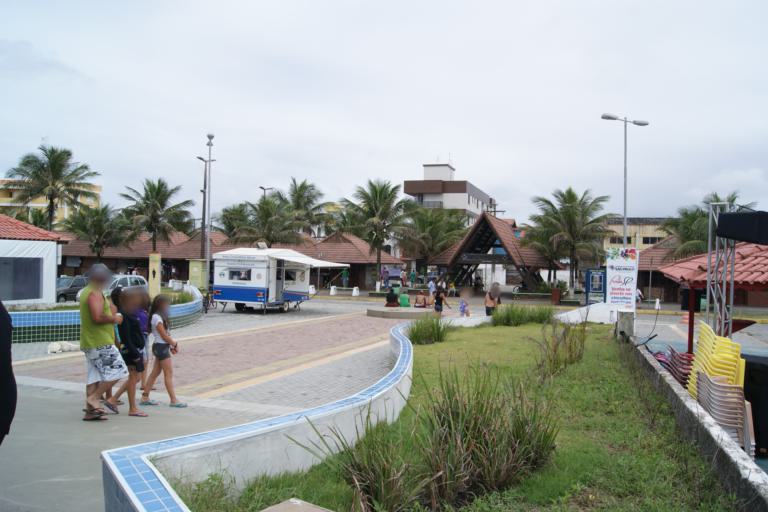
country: BR
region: Sao Paulo
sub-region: Mongagua
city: Mongagua
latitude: -24.1340
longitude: -46.6927
